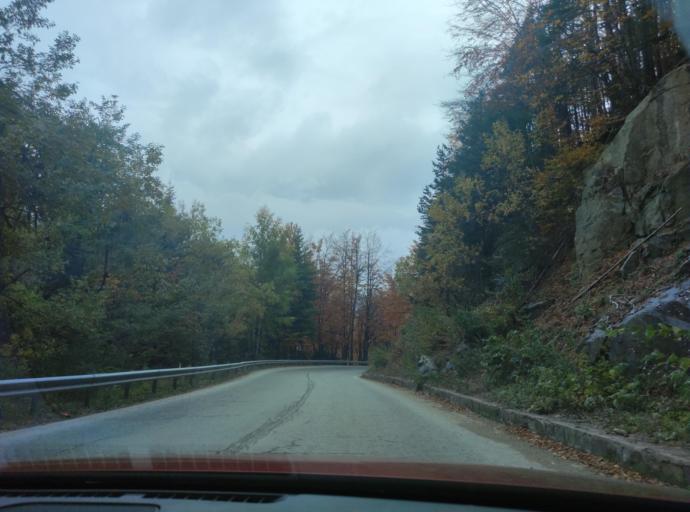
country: BG
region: Montana
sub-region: Obshtina Berkovitsa
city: Berkovitsa
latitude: 43.1331
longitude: 23.1459
